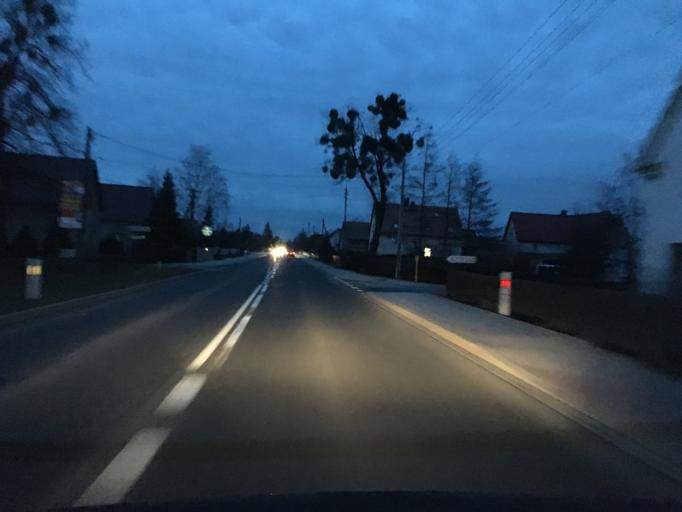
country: PL
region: Opole Voivodeship
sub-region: Powiat brzeski
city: Losiow
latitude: 50.7880
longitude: 17.5804
